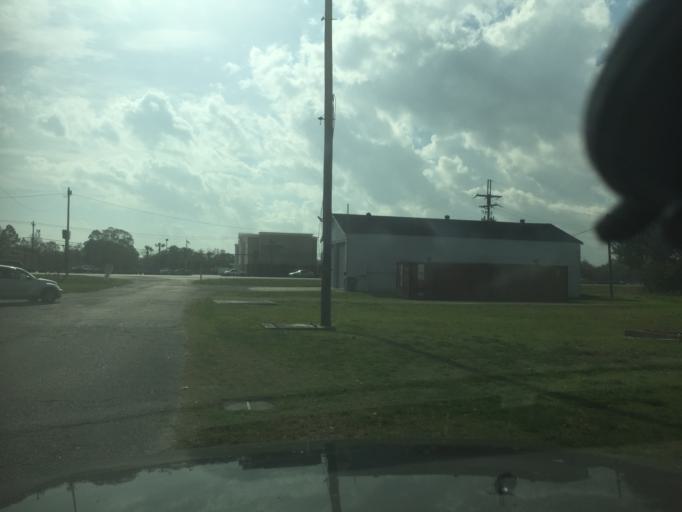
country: US
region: Louisiana
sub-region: Jefferson Parish
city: Avondale
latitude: 29.9110
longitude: -90.2068
